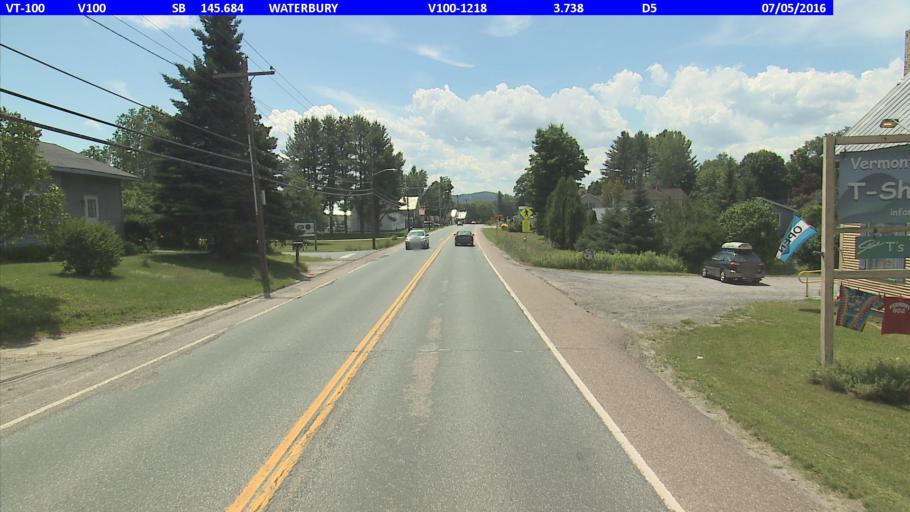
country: US
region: Vermont
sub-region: Washington County
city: Waterbury
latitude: 44.3833
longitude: -72.7208
